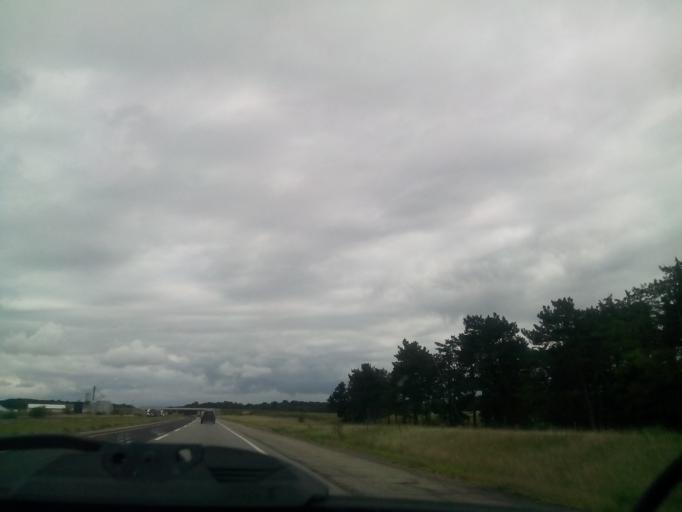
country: US
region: Michigan
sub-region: Saint Joseph County
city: Sturgis
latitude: 41.7444
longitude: -85.3234
